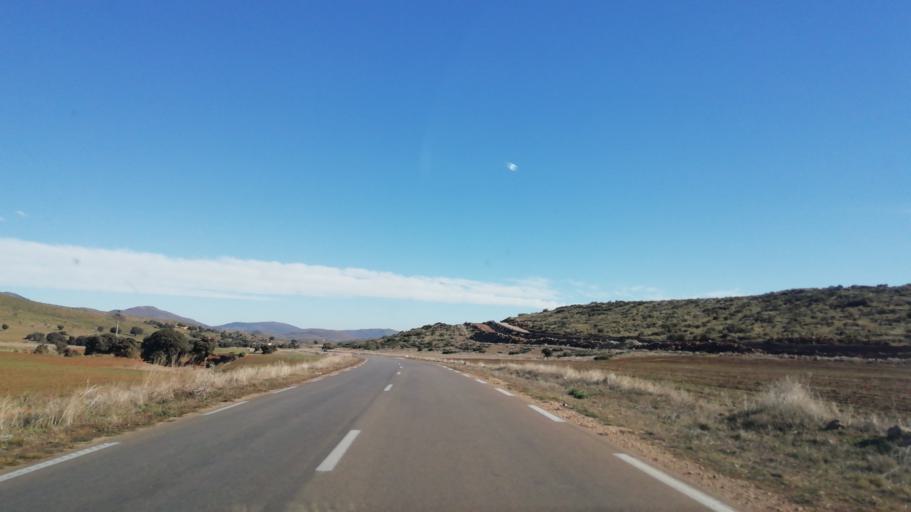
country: DZ
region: Tlemcen
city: Ouled Mimoun
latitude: 34.7501
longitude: -1.1578
